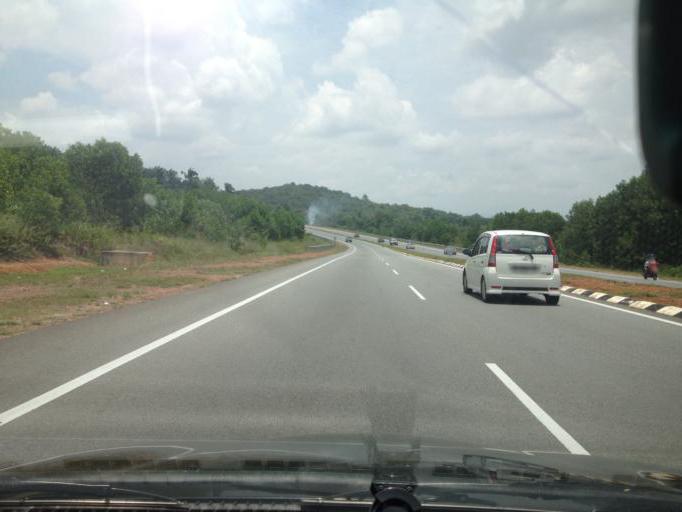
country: MY
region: Kedah
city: Sungai Petani
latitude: 5.6162
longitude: 100.5578
